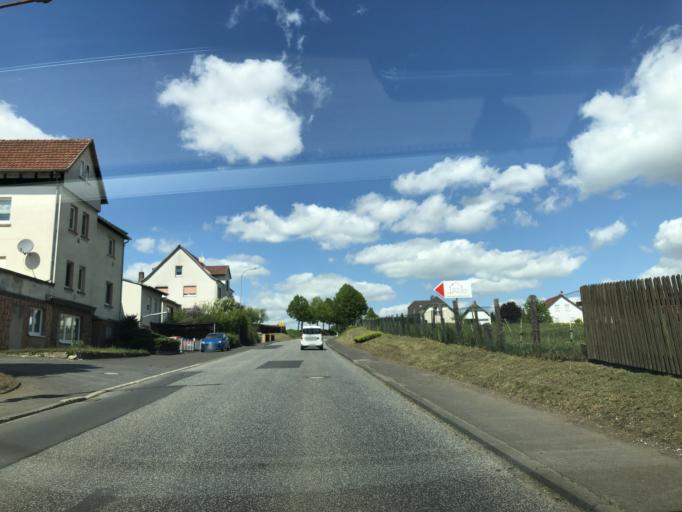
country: DE
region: Hesse
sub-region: Regierungsbezirk Kassel
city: Wabern
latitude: 51.1188
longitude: 9.3644
